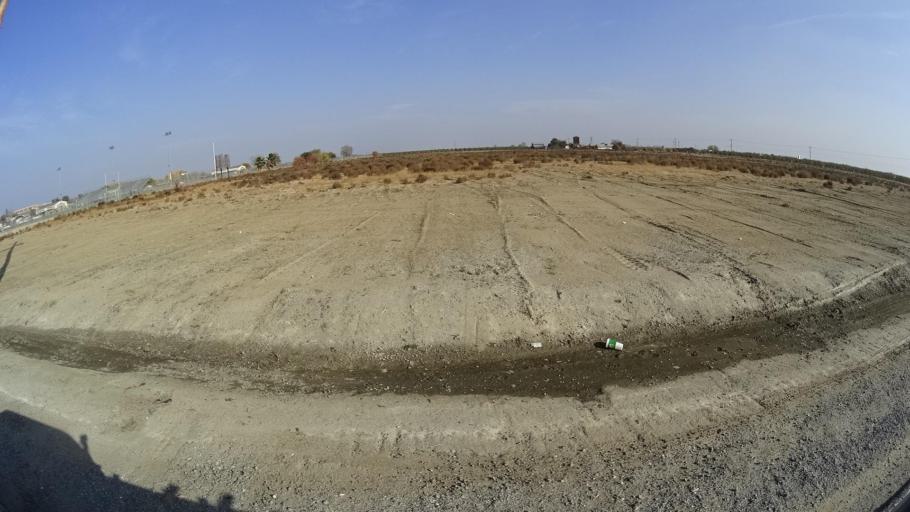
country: US
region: California
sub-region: Kern County
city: Delano
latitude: 35.7632
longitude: -119.2236
